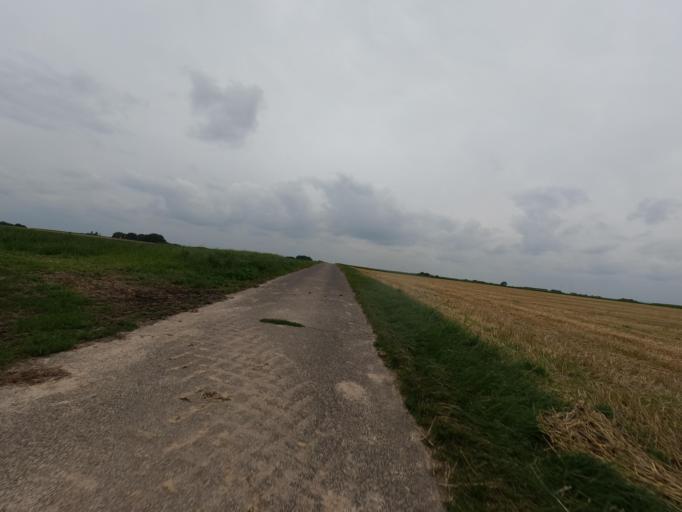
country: DE
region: North Rhine-Westphalia
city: Geilenkirchen
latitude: 50.9727
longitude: 6.1654
